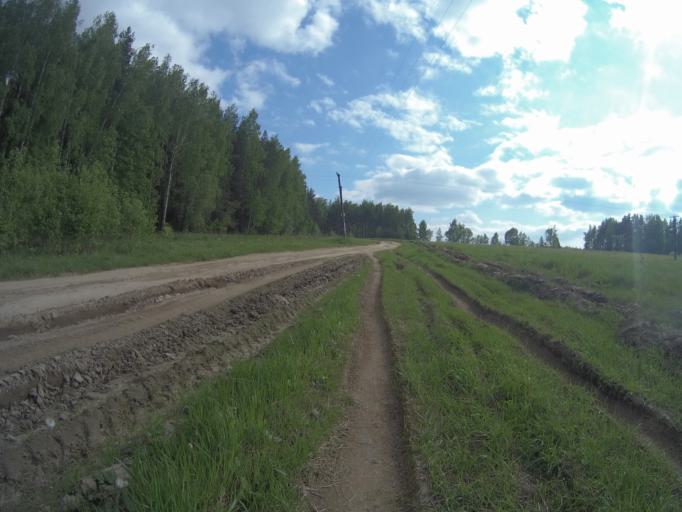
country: RU
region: Vladimir
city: Raduzhnyy
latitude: 55.9888
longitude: 40.2280
